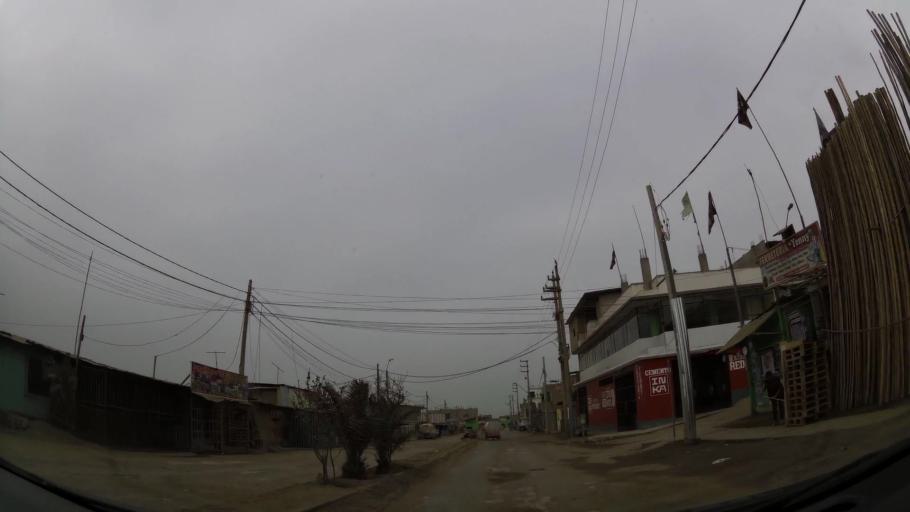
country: PE
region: Lima
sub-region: Lima
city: Surco
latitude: -12.2387
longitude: -76.9303
